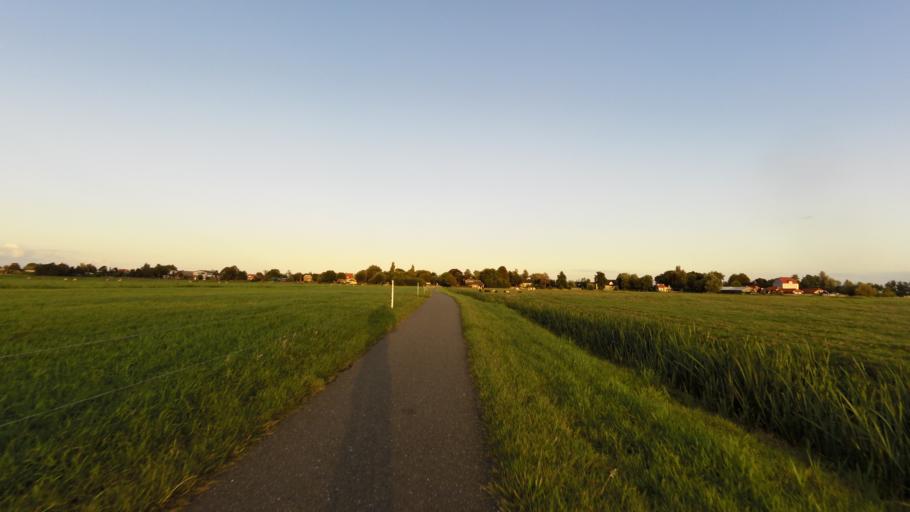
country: NL
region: South Holland
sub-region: Gemeente Rijnwoude
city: Benthuizen
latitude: 52.1081
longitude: 4.5137
